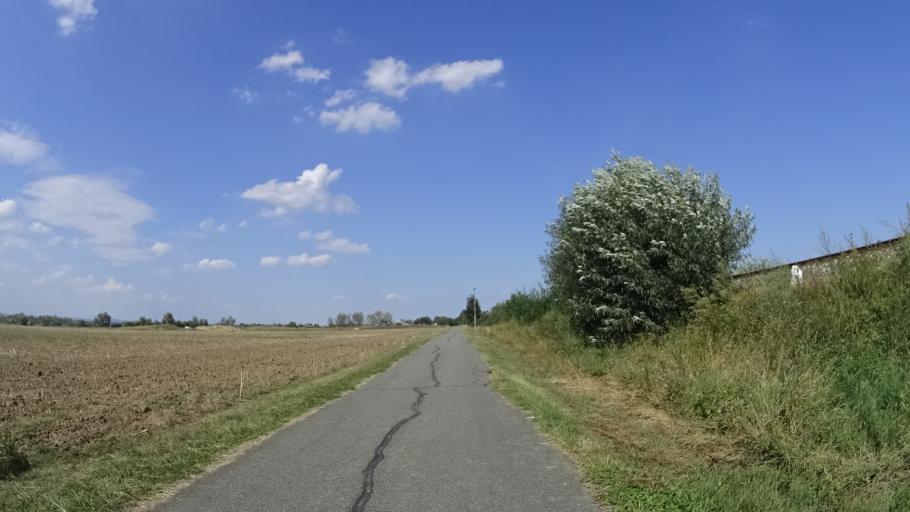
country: CZ
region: Zlin
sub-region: Okres Zlin
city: Ostrozska Nova Ves
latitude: 48.9969
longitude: 17.4212
